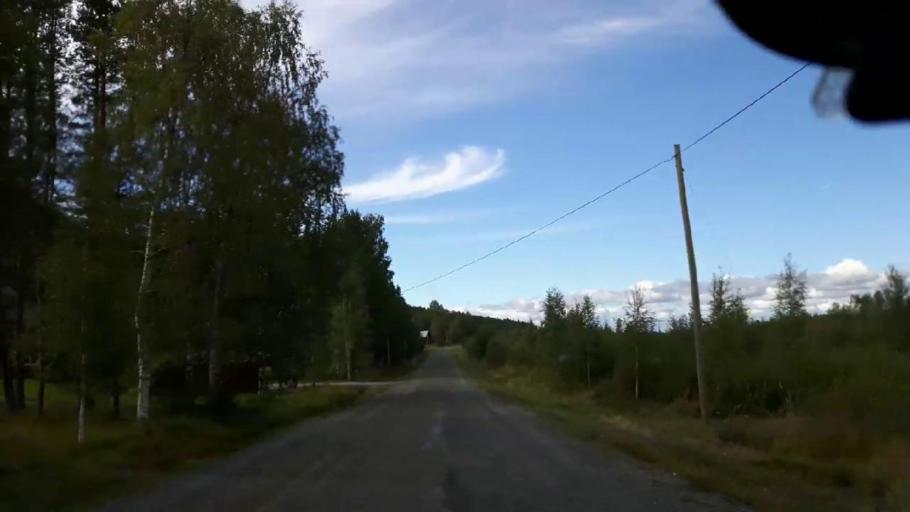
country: SE
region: Jaemtland
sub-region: Ragunda Kommun
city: Hammarstrand
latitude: 63.1176
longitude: 15.9998
